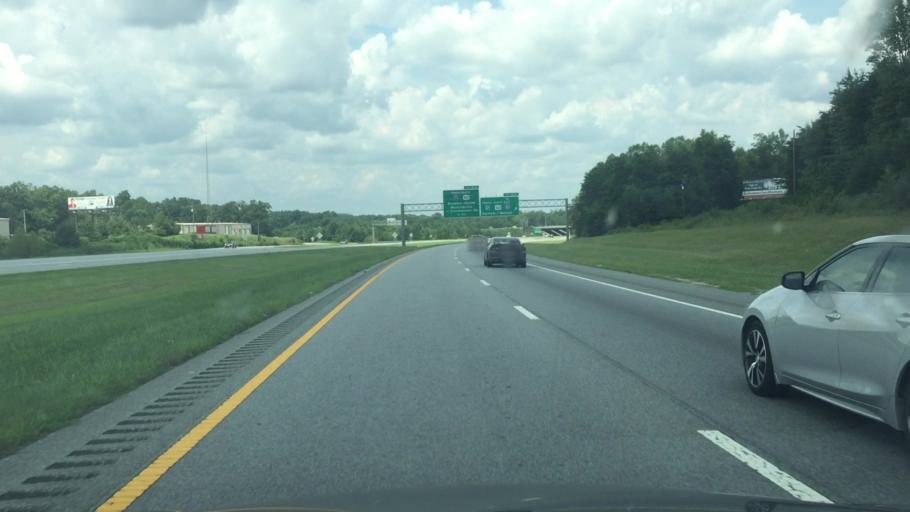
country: US
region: North Carolina
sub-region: Guilford County
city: Pleasant Garden
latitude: 35.9954
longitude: -79.8280
